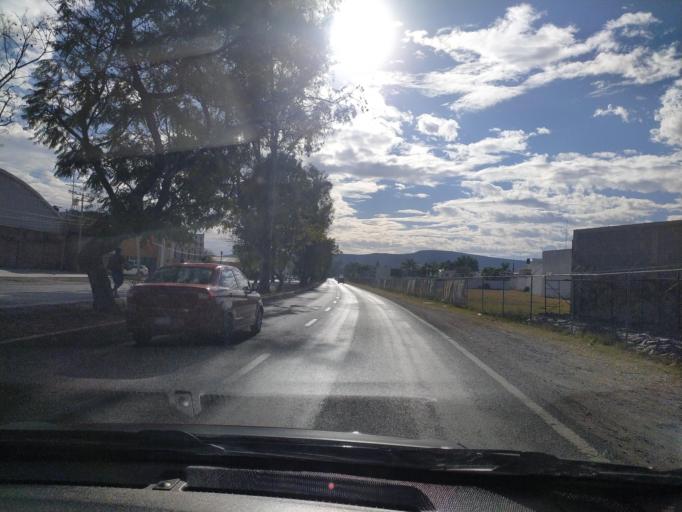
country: LA
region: Oudomxai
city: Muang La
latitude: 21.0316
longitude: 101.8417
